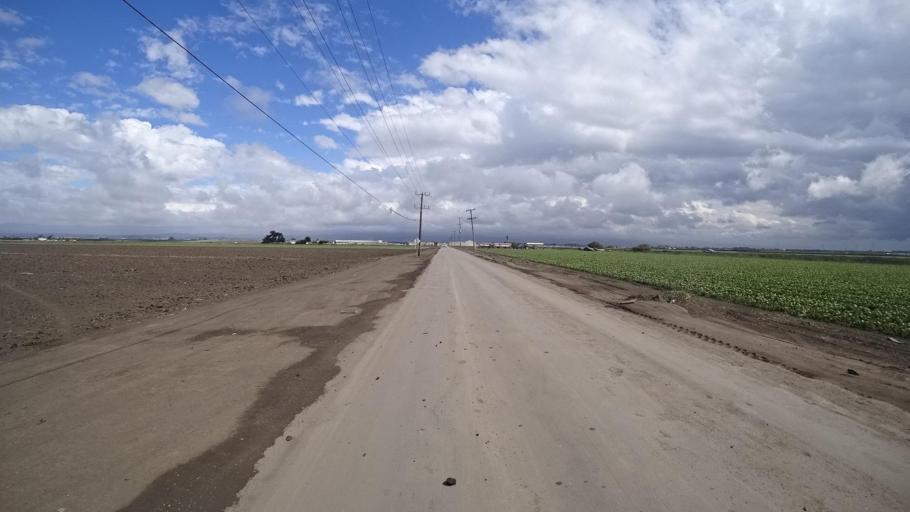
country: US
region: California
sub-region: Monterey County
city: Boronda
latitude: 36.6920
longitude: -121.7063
